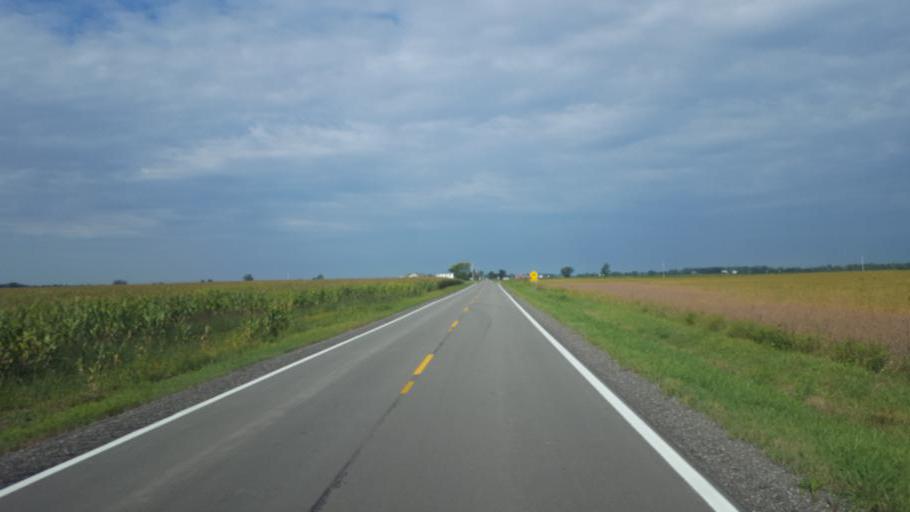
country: US
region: Ohio
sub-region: Marion County
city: Marion
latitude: 40.7174
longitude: -83.0885
